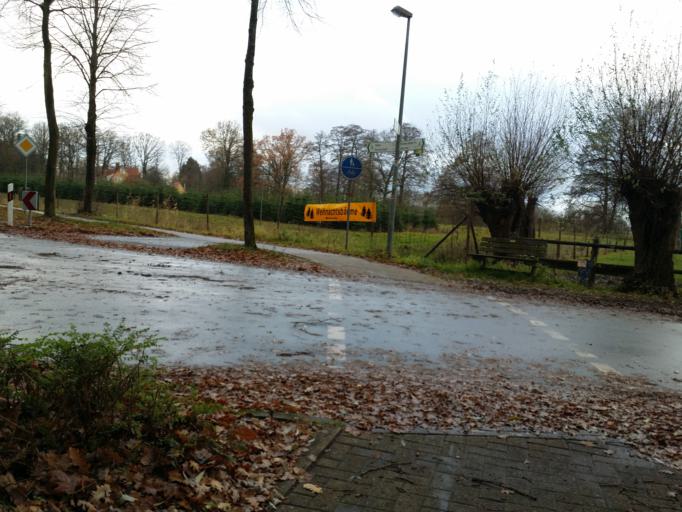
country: DE
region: Lower Saxony
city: Thedinghausen
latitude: 52.9659
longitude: 8.9895
